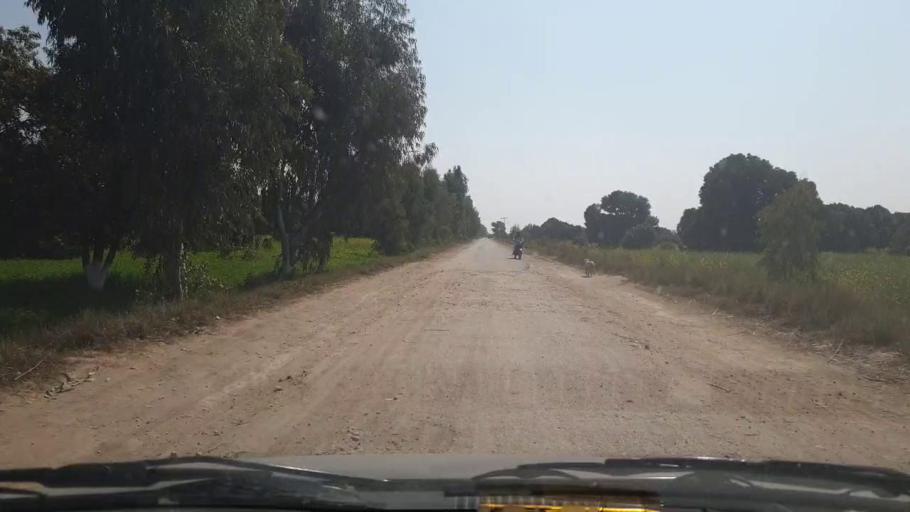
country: PK
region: Sindh
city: Samaro
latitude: 25.2681
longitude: 69.3473
